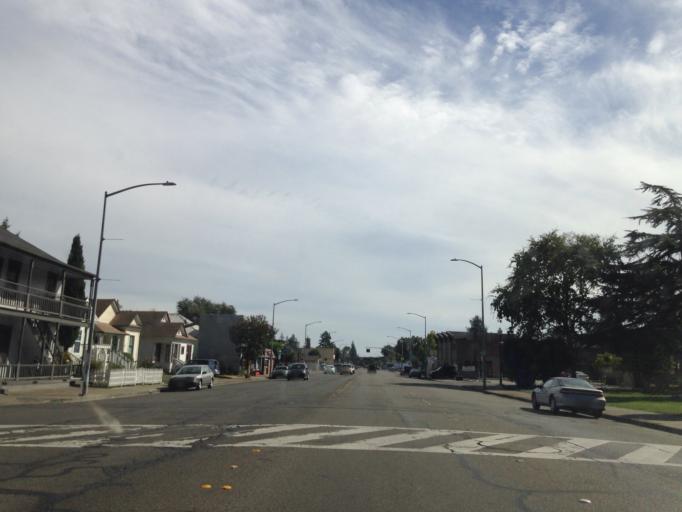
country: US
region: California
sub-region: Sonoma County
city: Santa Rosa
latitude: 38.4356
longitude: -122.7121
